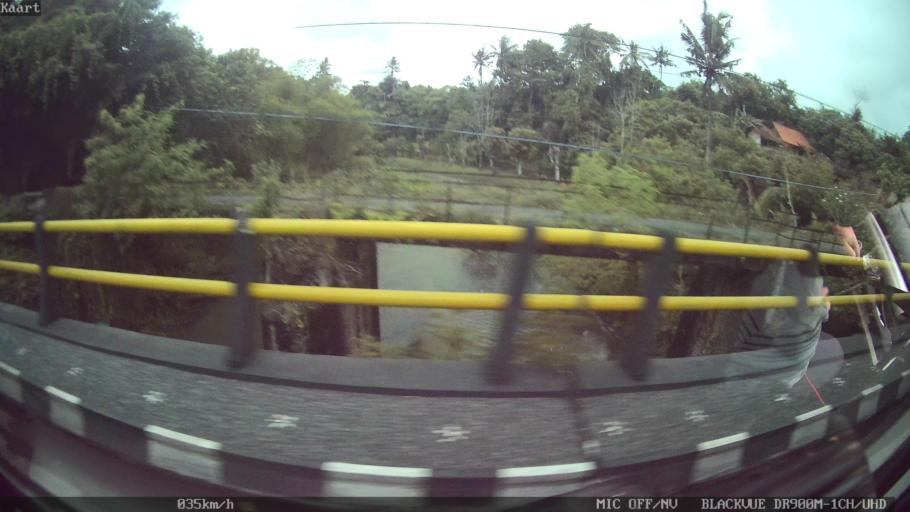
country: ID
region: Bali
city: Banjar Mambalkajanan
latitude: -8.5475
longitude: 115.2167
